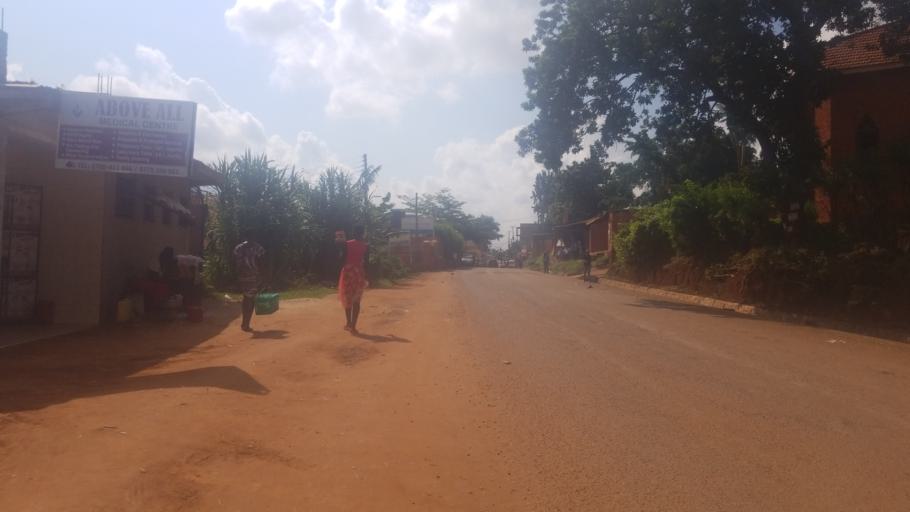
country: UG
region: Central Region
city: Kampala Central Division
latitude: 0.3337
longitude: 32.5627
